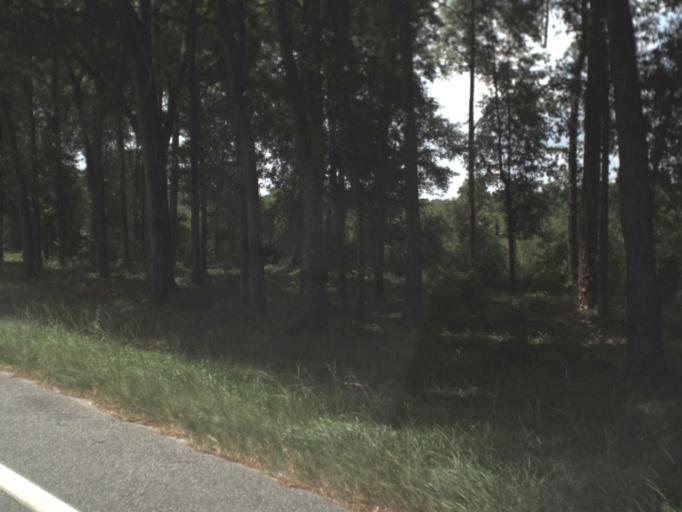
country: US
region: Florida
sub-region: Hamilton County
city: Jasper
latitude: 30.5268
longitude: -83.0319
